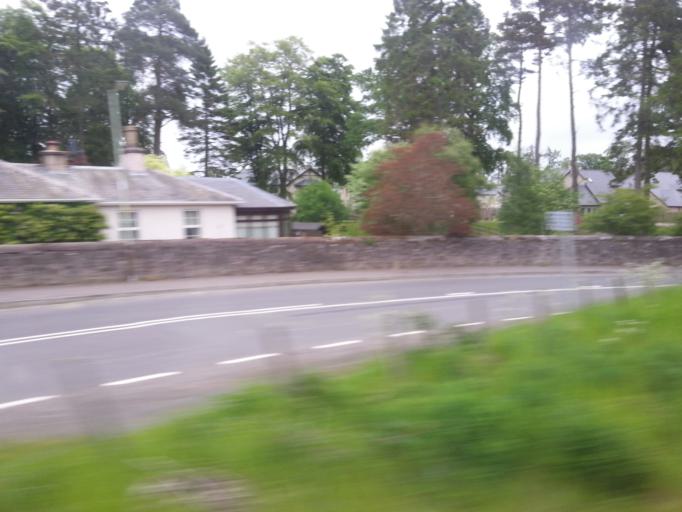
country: GB
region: Scotland
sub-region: Perth and Kinross
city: Stanley
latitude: 56.5282
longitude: -3.4623
